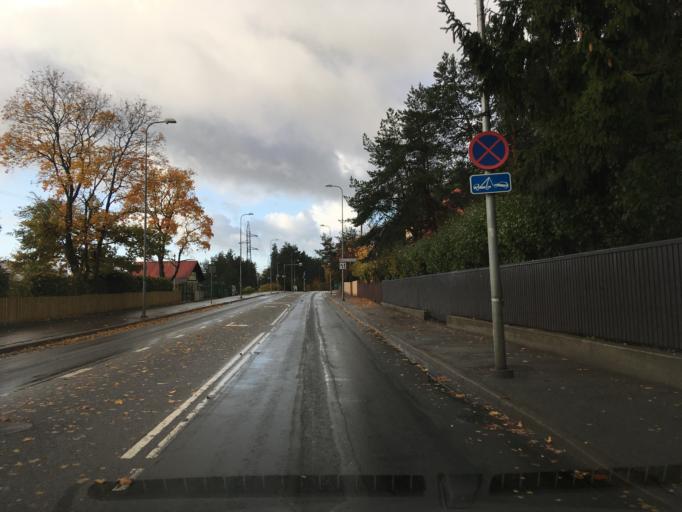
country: EE
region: Harju
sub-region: Saue vald
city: Laagri
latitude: 59.3671
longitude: 24.6346
